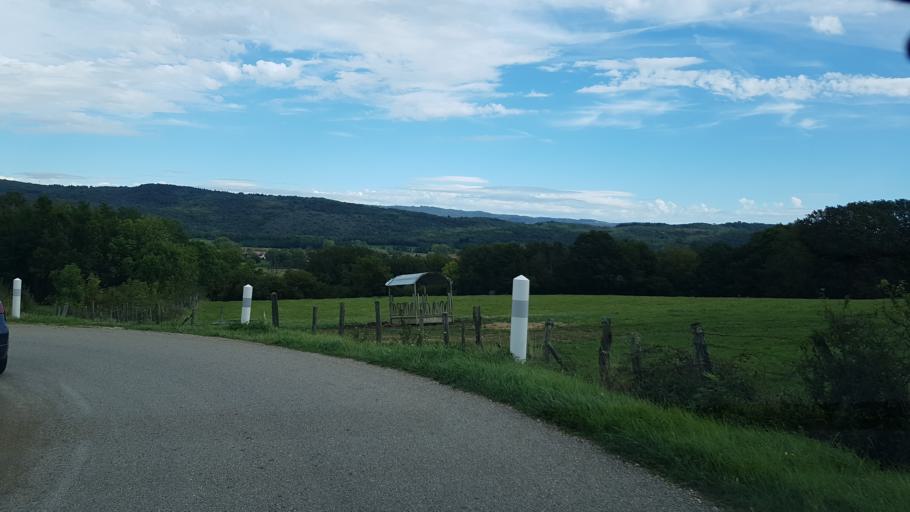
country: FR
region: Rhone-Alpes
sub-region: Departement de l'Ain
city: Villereversure
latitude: 46.1800
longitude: 5.3771
